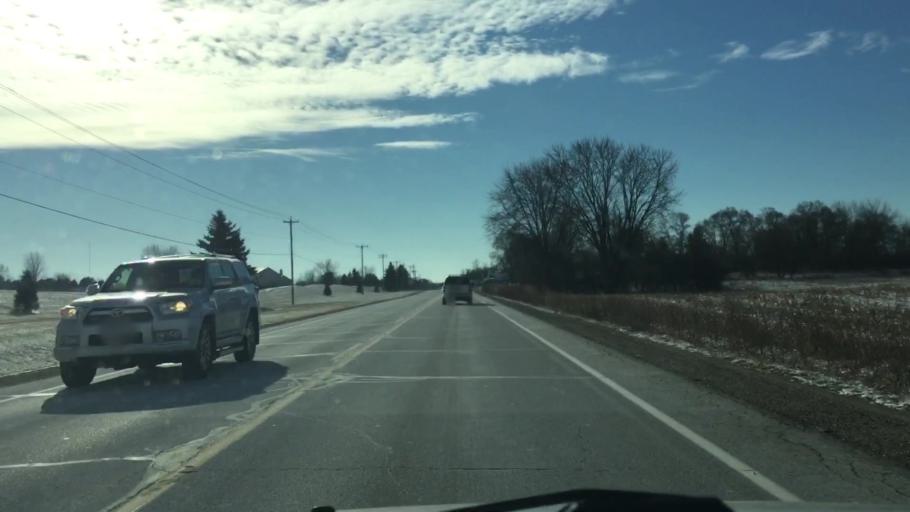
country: US
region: Wisconsin
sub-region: Walworth County
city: Elkhorn
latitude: 42.7519
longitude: -88.5536
